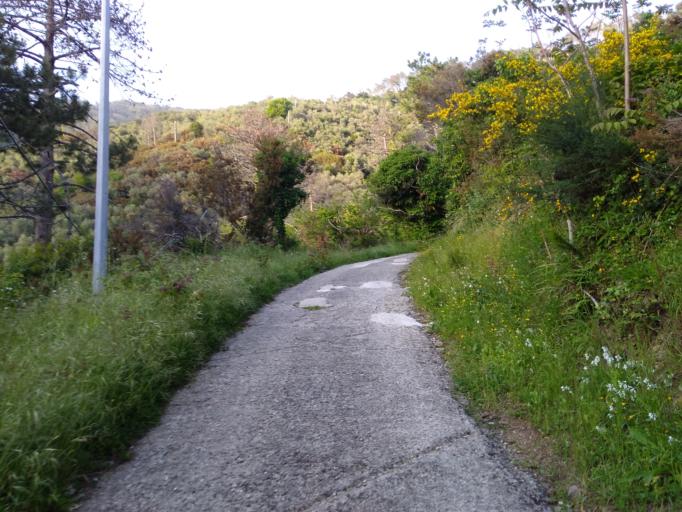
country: IT
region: Liguria
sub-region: Provincia di La Spezia
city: Monterosso al Mare
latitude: 44.1540
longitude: 9.6564
